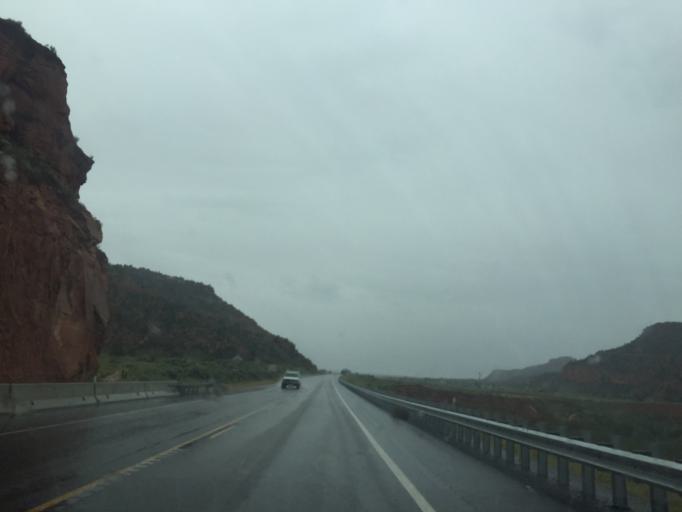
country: US
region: Utah
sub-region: Kane County
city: Kanab
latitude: 37.0715
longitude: -112.5368
